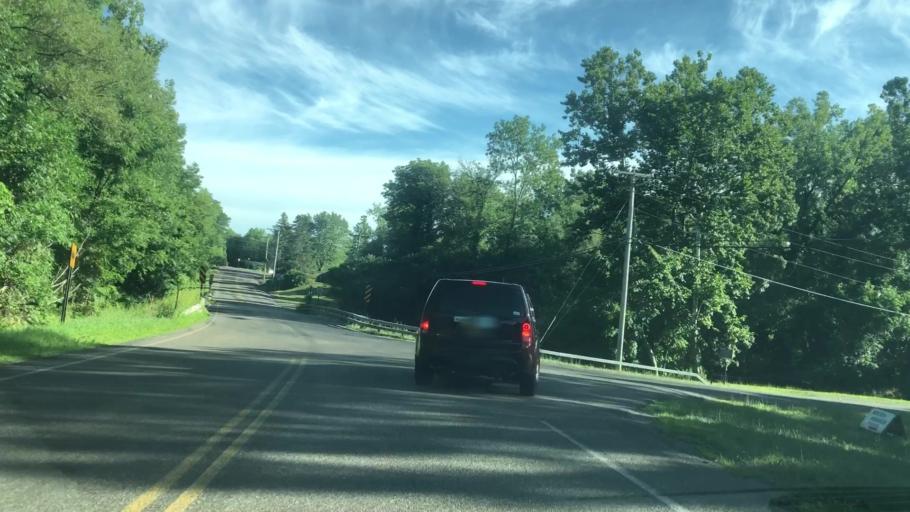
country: US
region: New York
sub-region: Wayne County
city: Macedon
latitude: 43.0444
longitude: -77.3405
